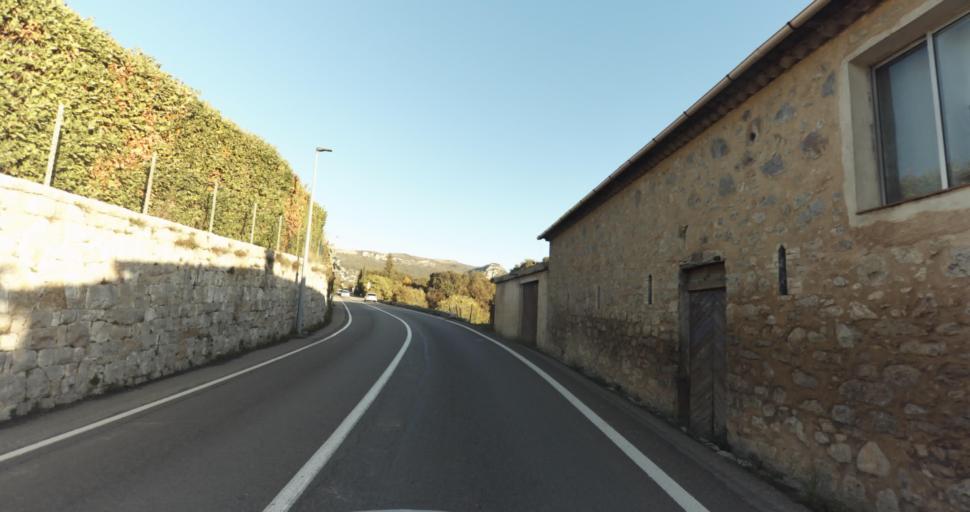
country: FR
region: Provence-Alpes-Cote d'Azur
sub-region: Departement des Alpes-Maritimes
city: Saint-Paul-de-Vence
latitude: 43.7094
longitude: 7.1309
